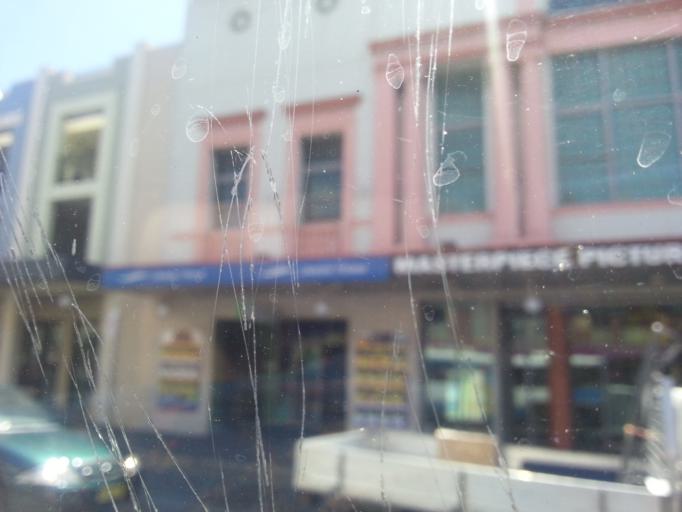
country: AU
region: New South Wales
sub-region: Marrickville
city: Newtown
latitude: -33.9065
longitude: 151.1813
